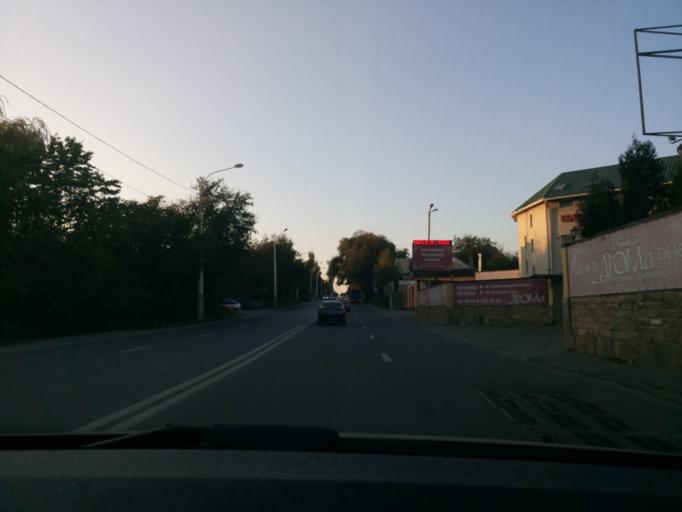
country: RU
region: Rostov
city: Rostov-na-Donu
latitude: 47.2289
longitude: 39.6465
